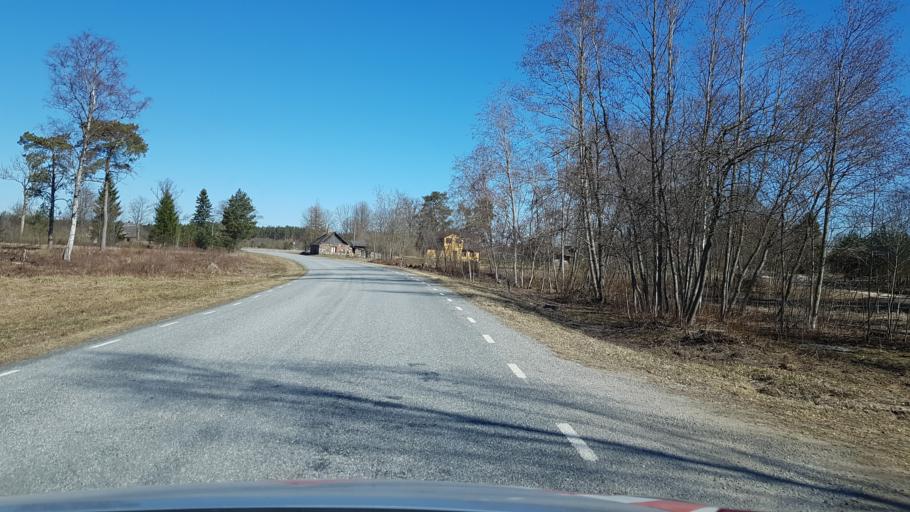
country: EE
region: Laeaene-Virumaa
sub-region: Haljala vald
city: Haljala
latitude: 59.4652
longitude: 26.2417
